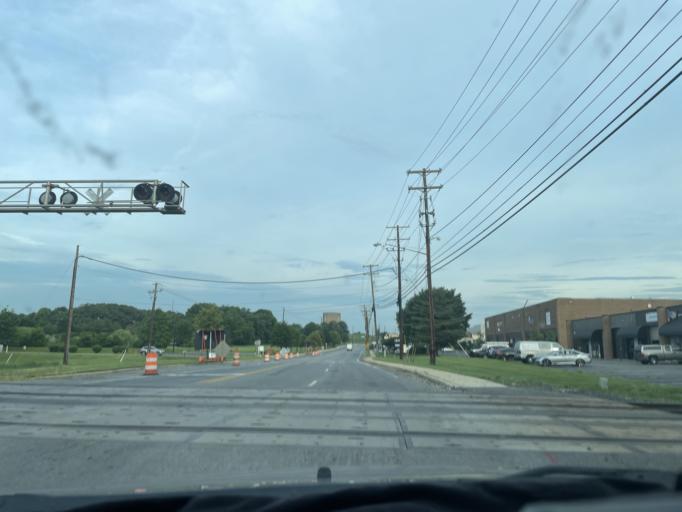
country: US
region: Maryland
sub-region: Prince George's County
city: Beltsville
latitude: 39.0231
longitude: -76.9069
